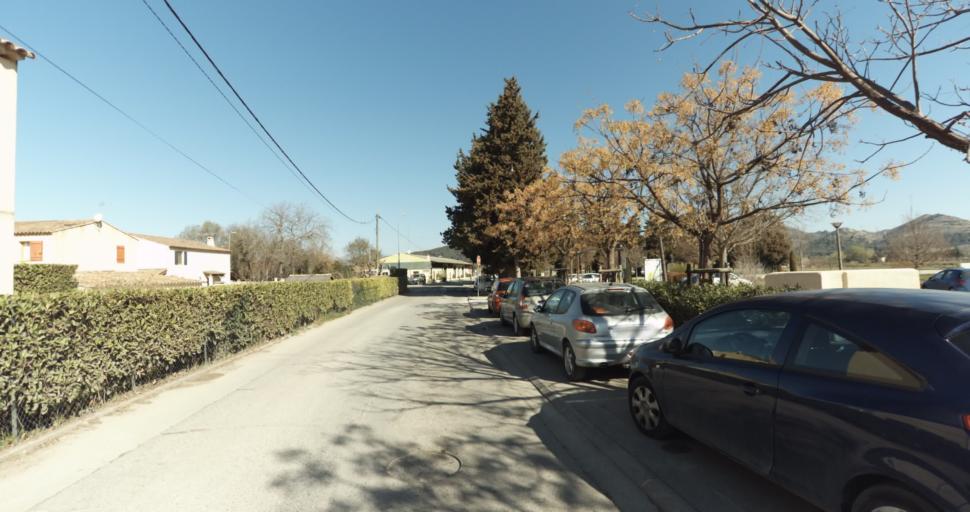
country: FR
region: Provence-Alpes-Cote d'Azur
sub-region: Departement des Bouches-du-Rhone
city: Peyrolles-en-Provence
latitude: 43.6484
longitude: 5.5813
